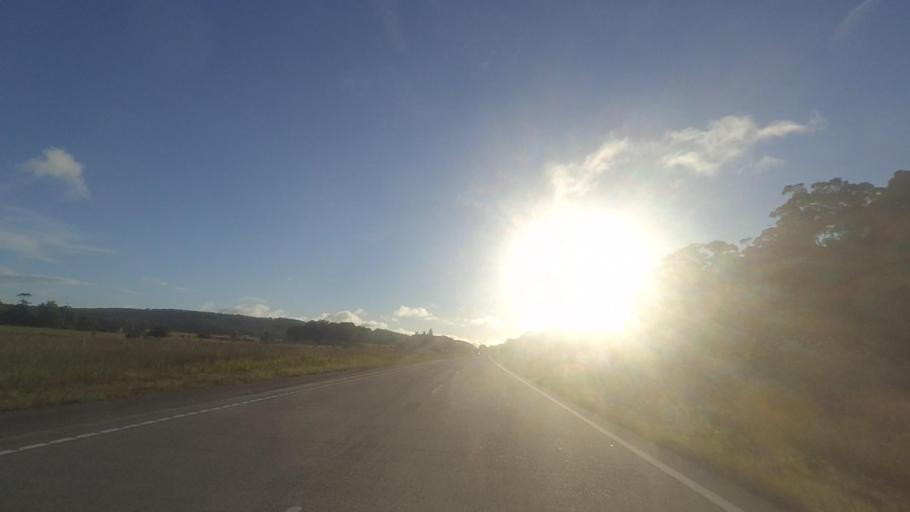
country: AU
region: New South Wales
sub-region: Great Lakes
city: Bulahdelah
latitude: -32.5224
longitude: 152.2011
